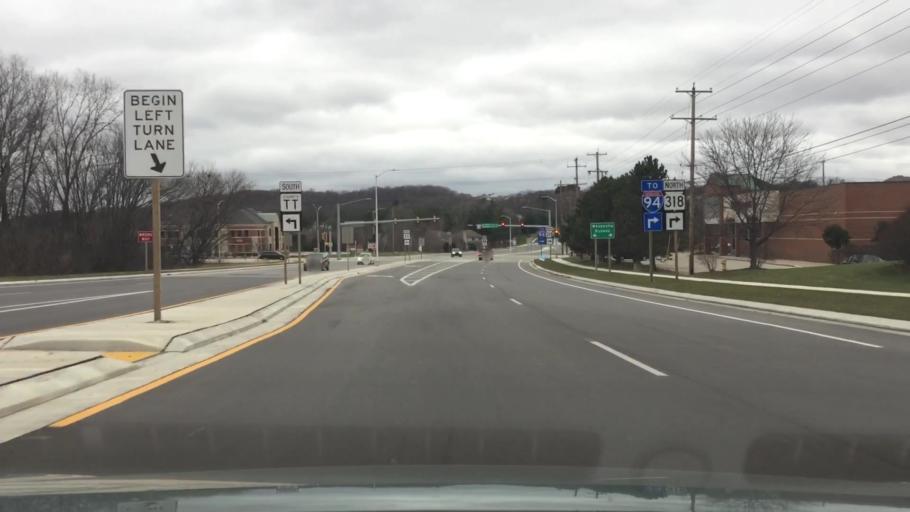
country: US
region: Wisconsin
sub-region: Waukesha County
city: Waukesha
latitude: 43.0206
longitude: -88.2839
